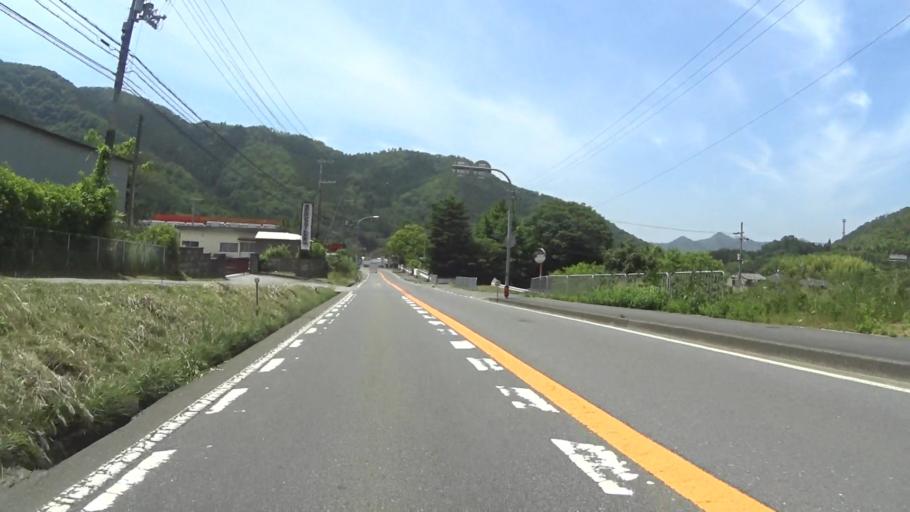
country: JP
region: Kyoto
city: Ayabe
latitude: 35.2311
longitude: 135.2237
